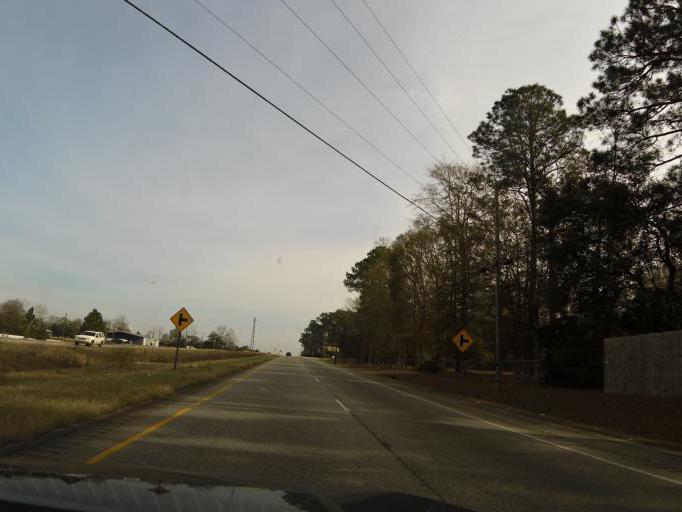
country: US
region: Alabama
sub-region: Houston County
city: Cowarts
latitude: 31.1949
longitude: -85.3270
